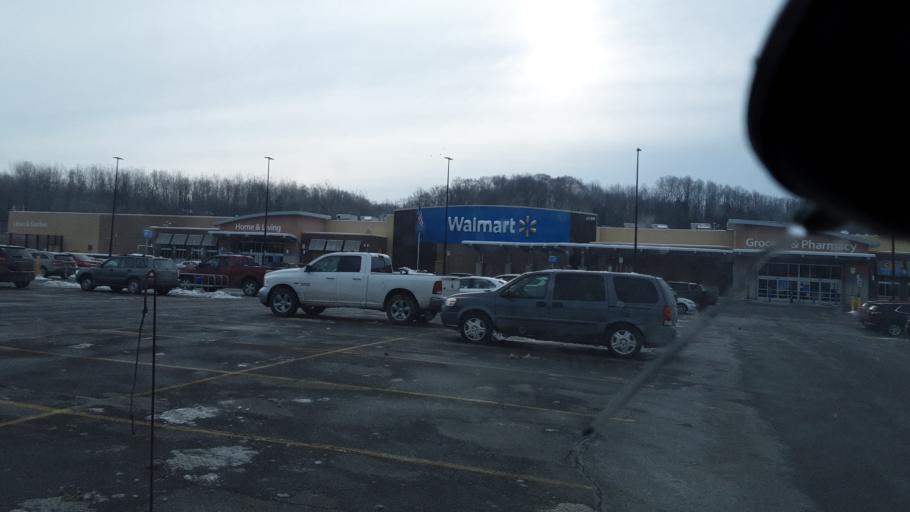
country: US
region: New York
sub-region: Wayne County
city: Newark
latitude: 43.0525
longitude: -77.0590
